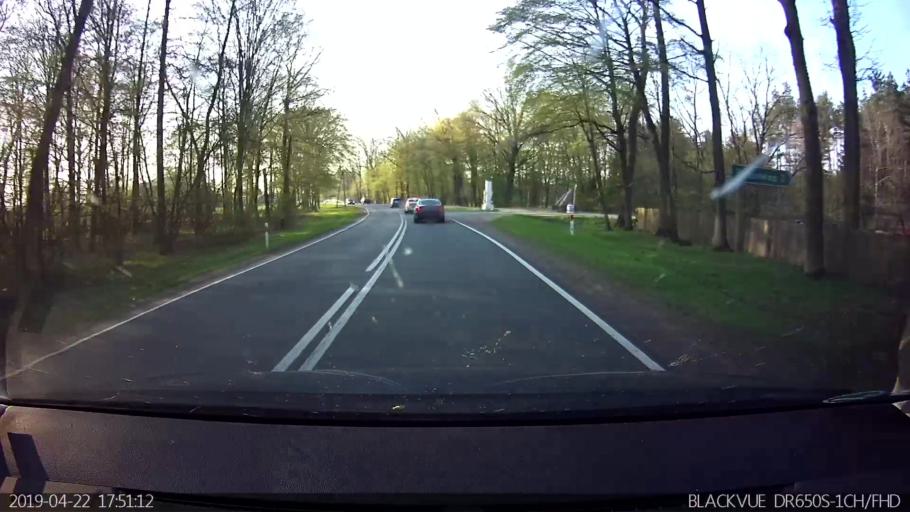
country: PL
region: Masovian Voivodeship
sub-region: Powiat wegrowski
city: Wegrow
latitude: 52.4334
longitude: 21.9961
